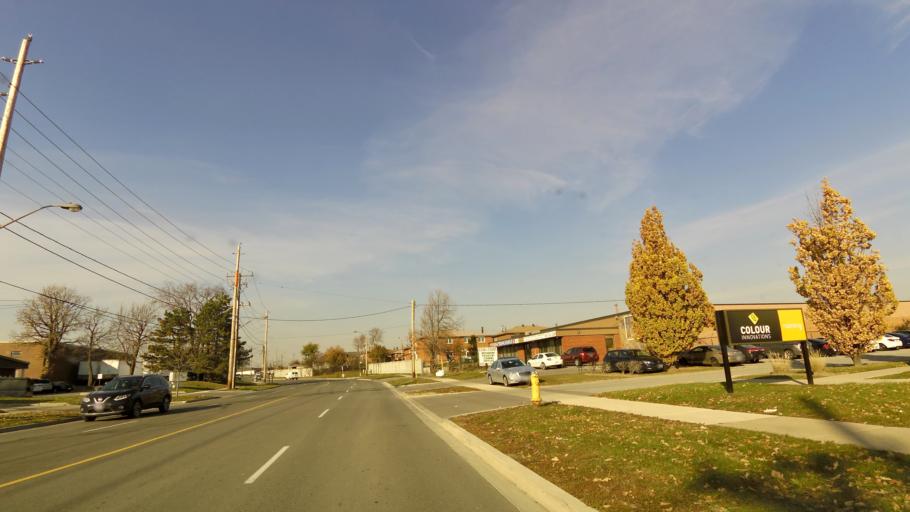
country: CA
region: Ontario
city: Concord
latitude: 43.7655
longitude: -79.5301
